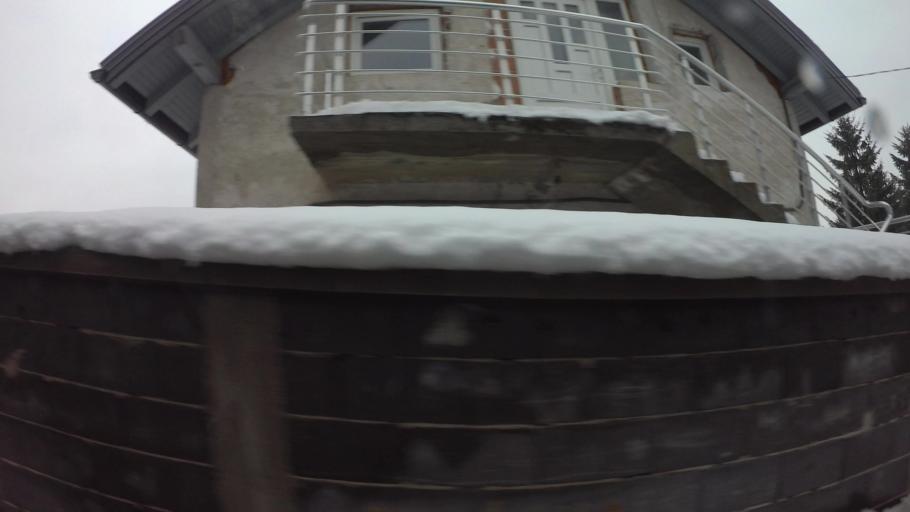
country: BA
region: Federation of Bosnia and Herzegovina
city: Hadzici
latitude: 43.8481
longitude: 18.2569
